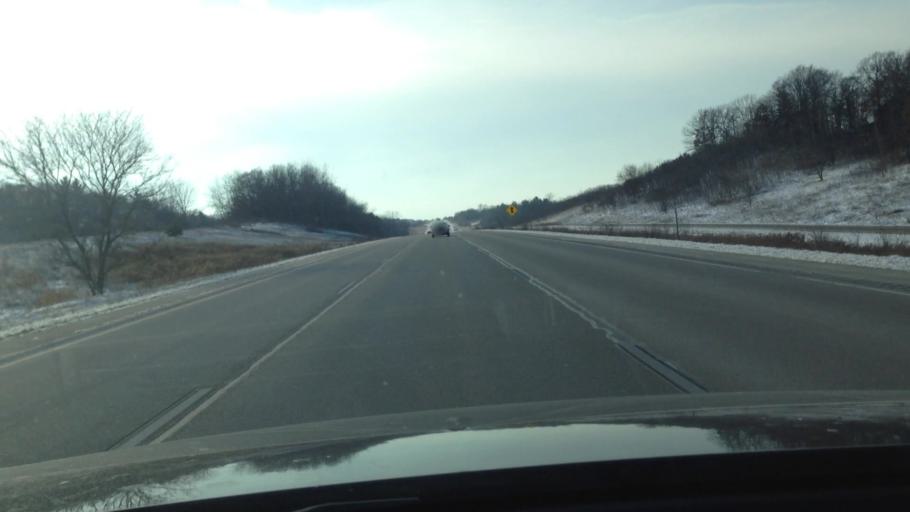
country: US
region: Wisconsin
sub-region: Walworth County
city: East Troy
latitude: 42.7735
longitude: -88.4079
